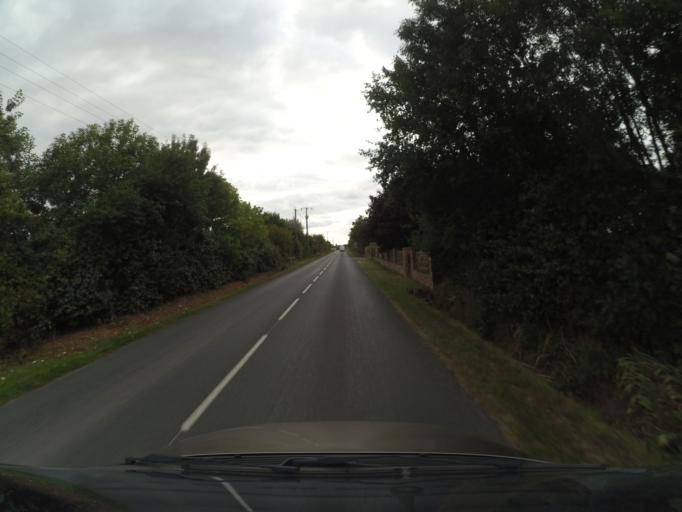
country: FR
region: Pays de la Loire
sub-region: Departement de la Vendee
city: Saint-Andre-Treize-Voies
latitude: 46.9193
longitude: -1.3900
